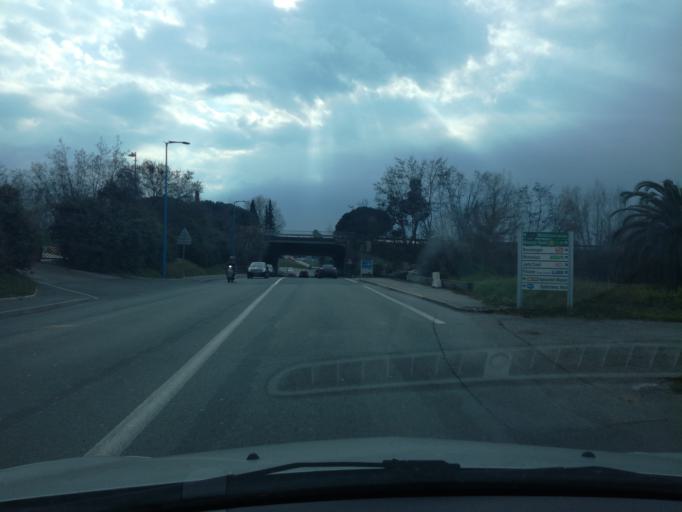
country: FR
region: Provence-Alpes-Cote d'Azur
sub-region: Departement des Alpes-Maritimes
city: Mandelieu-la-Napoule
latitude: 43.5590
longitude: 6.9514
